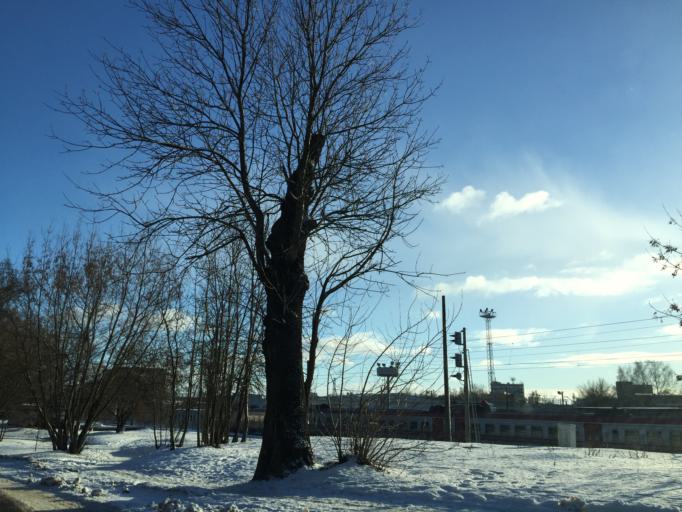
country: LV
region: Riga
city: Riga
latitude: 56.9451
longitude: 24.1547
